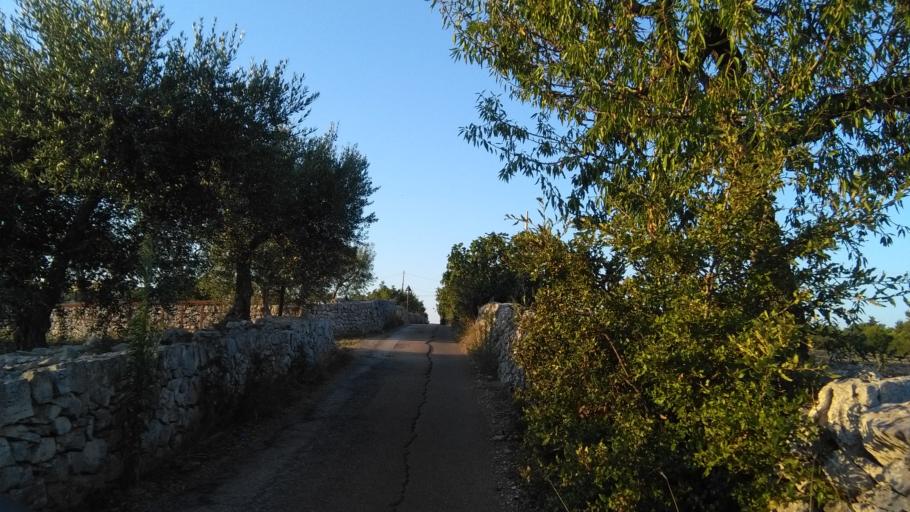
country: IT
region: Apulia
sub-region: Provincia di Bari
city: Putignano
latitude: 40.8232
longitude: 17.1028
